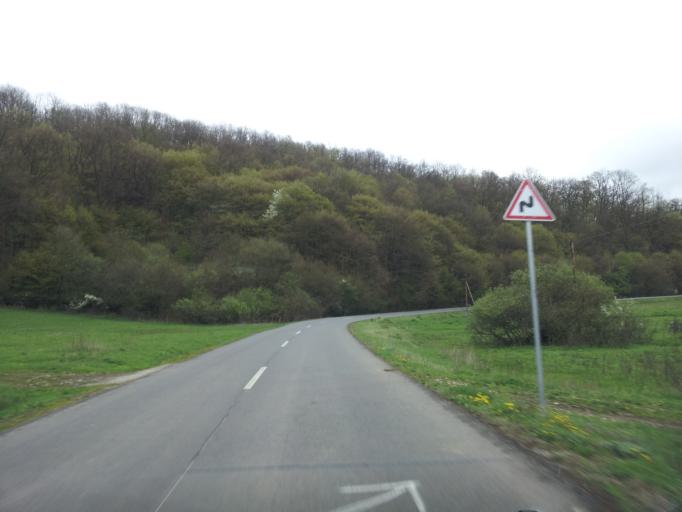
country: HU
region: Borsod-Abauj-Zemplen
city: Rudabanya
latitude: 48.4801
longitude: 20.5703
